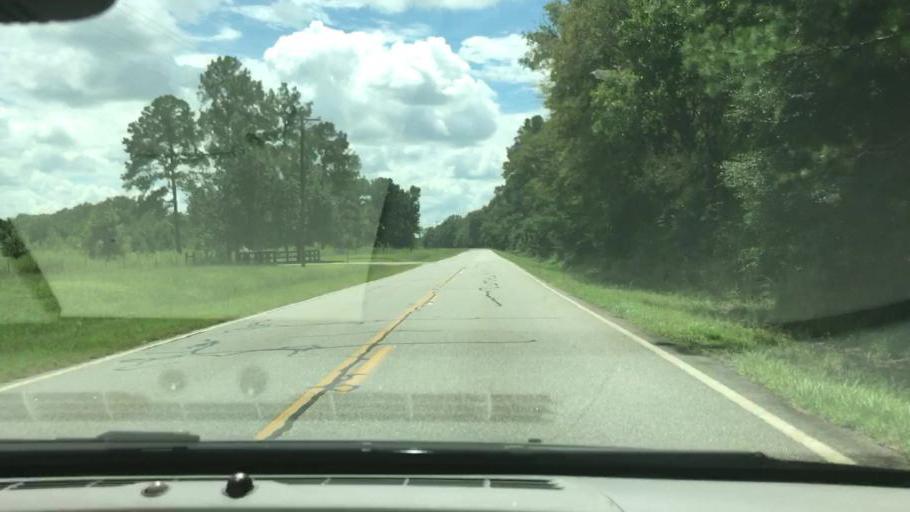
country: US
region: Georgia
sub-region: Quitman County
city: Georgetown
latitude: 32.1159
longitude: -85.0371
